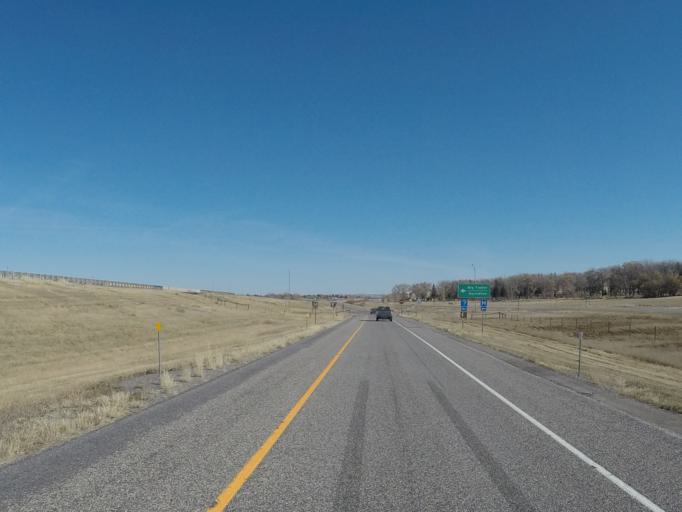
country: US
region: Montana
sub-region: Sweet Grass County
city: Big Timber
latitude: 45.8244
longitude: -109.9748
